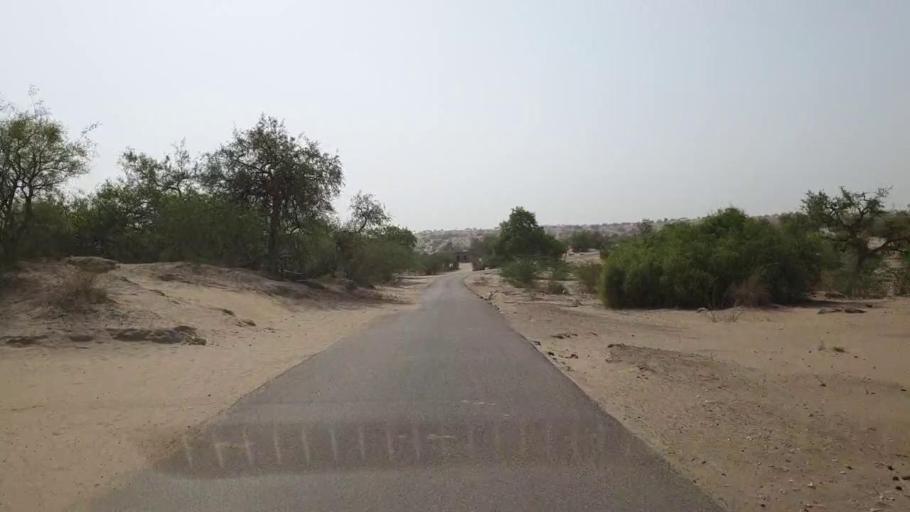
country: PK
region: Sindh
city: Mithi
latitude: 24.5769
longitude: 69.9270
